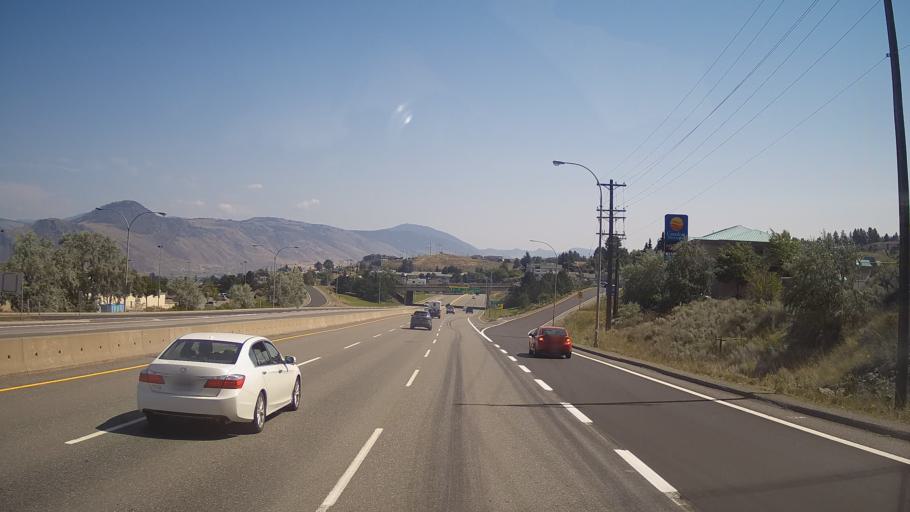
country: CA
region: British Columbia
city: Kamloops
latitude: 50.6530
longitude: -120.3729
